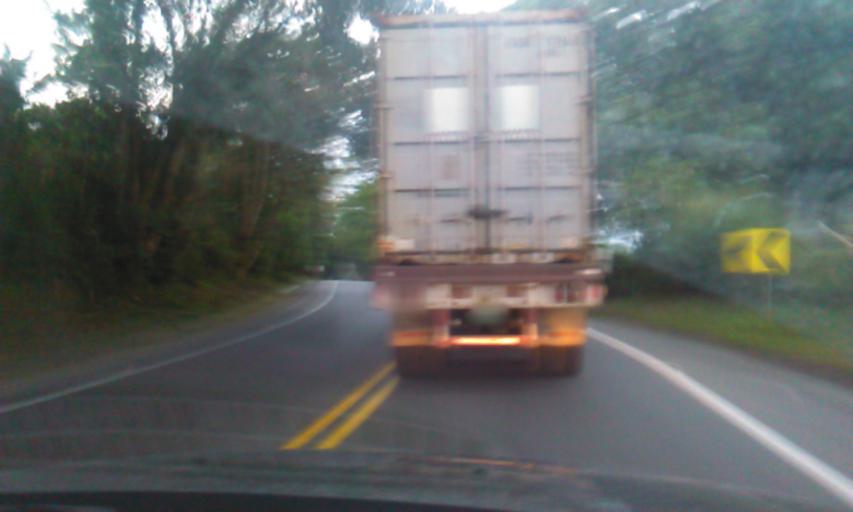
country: CO
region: Quindio
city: La Tebaida
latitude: 4.4478
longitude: -75.8091
